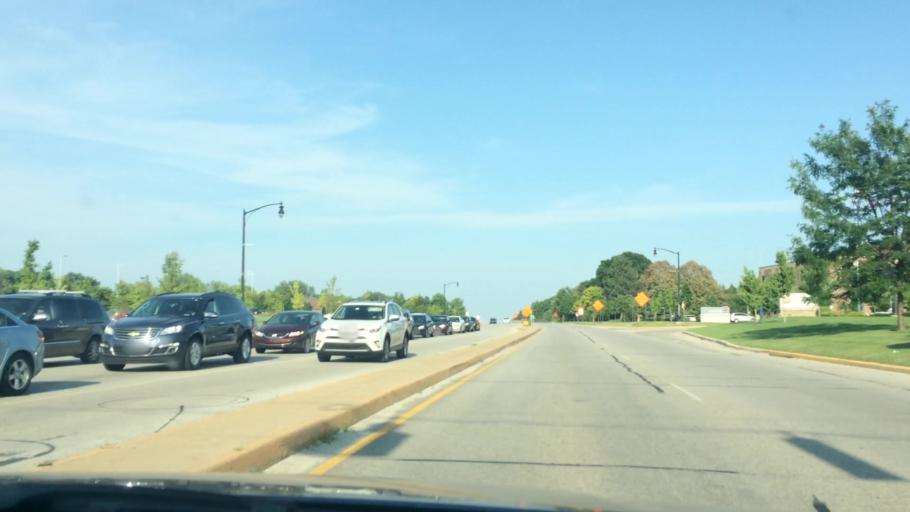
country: US
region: Indiana
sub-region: Tippecanoe County
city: West Lafayette
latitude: 40.4530
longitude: -86.9107
